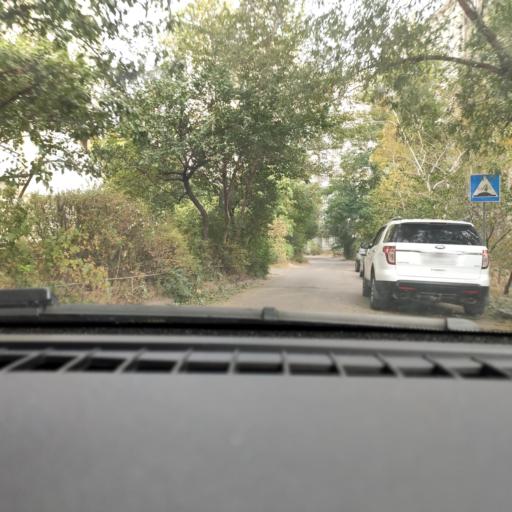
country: RU
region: Voronezj
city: Voronezh
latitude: 51.6803
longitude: 39.2507
